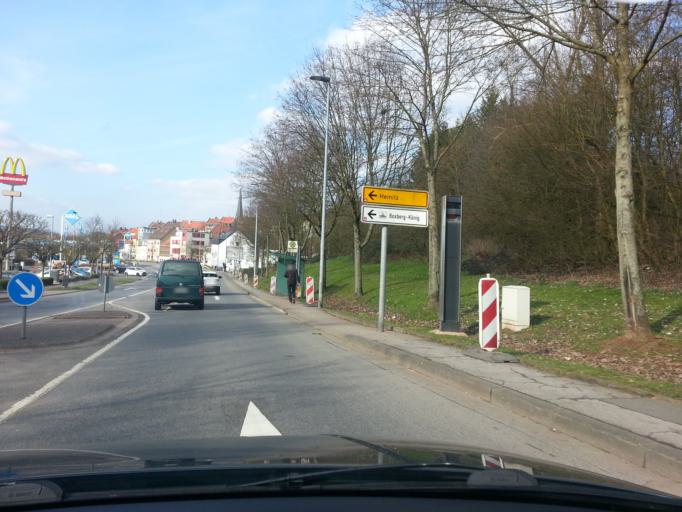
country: DE
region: Saarland
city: Neunkirchen
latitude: 49.3430
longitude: 7.1745
